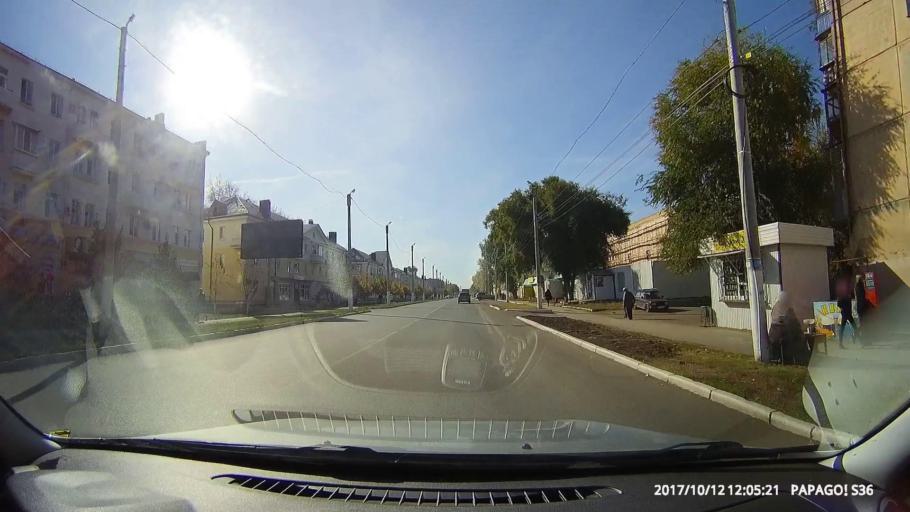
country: RU
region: Samara
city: Chapayevsk
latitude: 52.9776
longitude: 49.7125
